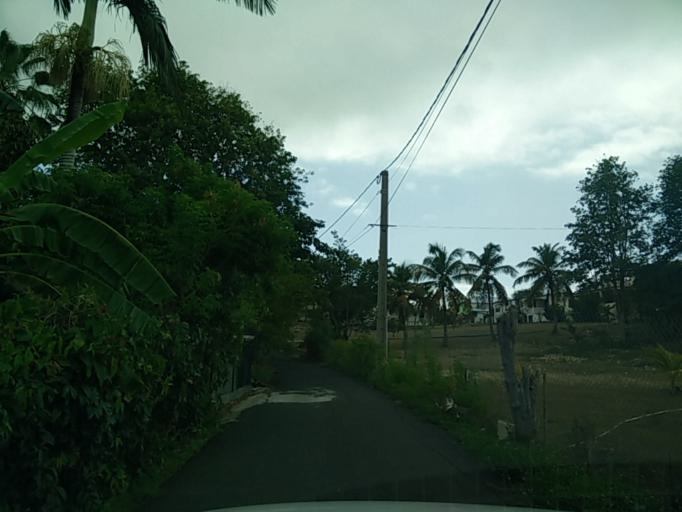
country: GP
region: Guadeloupe
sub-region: Guadeloupe
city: Sainte-Anne
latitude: 16.2200
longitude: -61.4018
